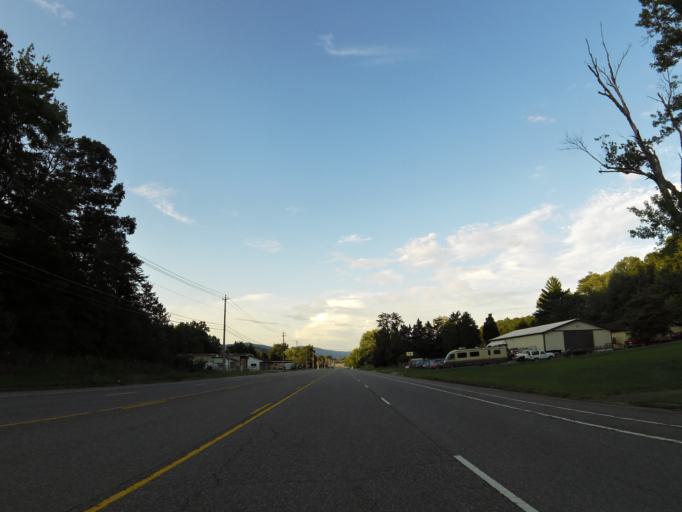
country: US
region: Tennessee
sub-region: Grainger County
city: Blaine
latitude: 36.1454
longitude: -83.7119
